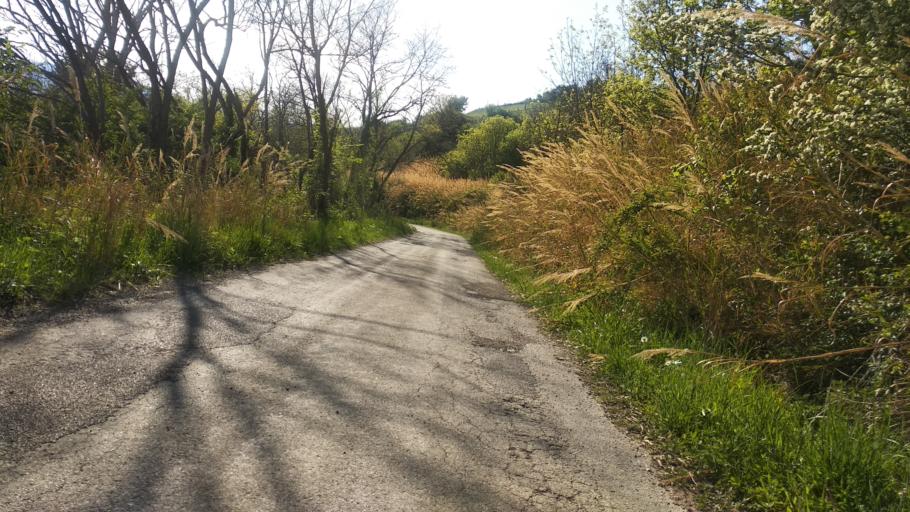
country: IT
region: Emilia-Romagna
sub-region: Provincia di Ravenna
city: Fognano
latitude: 44.2234
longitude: 11.7306
